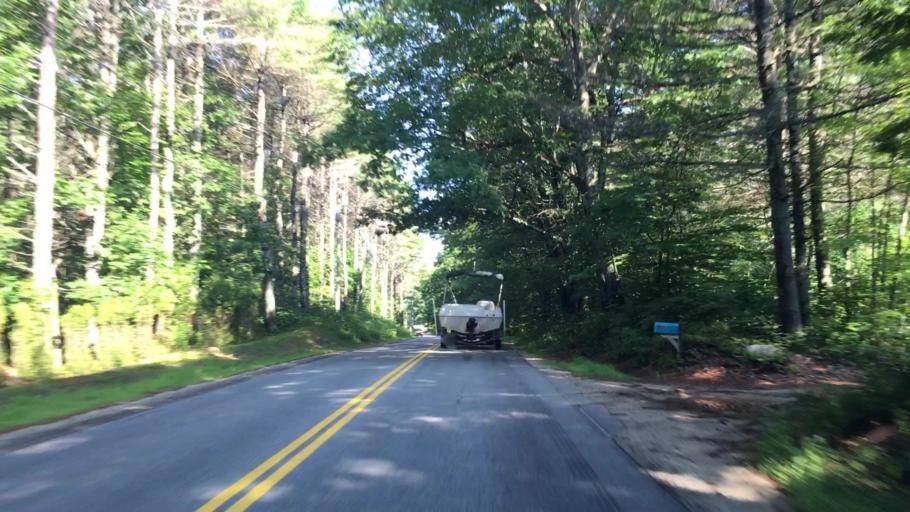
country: US
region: Maine
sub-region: Androscoggin County
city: Poland
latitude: 44.0563
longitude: -70.3795
